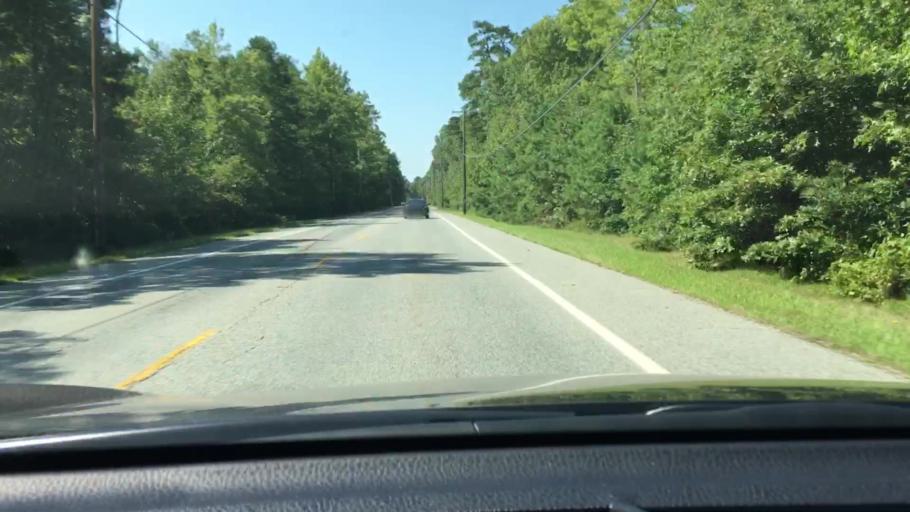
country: US
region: New Jersey
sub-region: Cape May County
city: Woodbine
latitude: 39.2903
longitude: -74.7865
